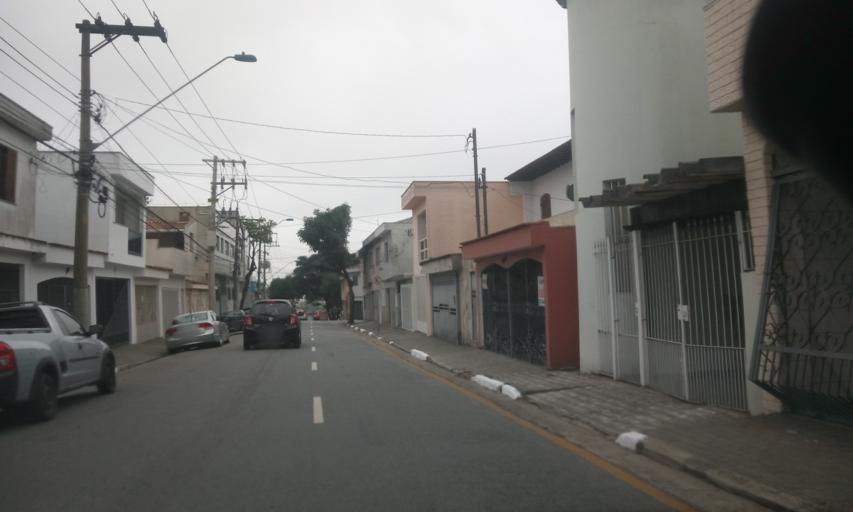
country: BR
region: Sao Paulo
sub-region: Sao Caetano Do Sul
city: Sao Caetano do Sul
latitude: -23.6365
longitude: -46.5691
